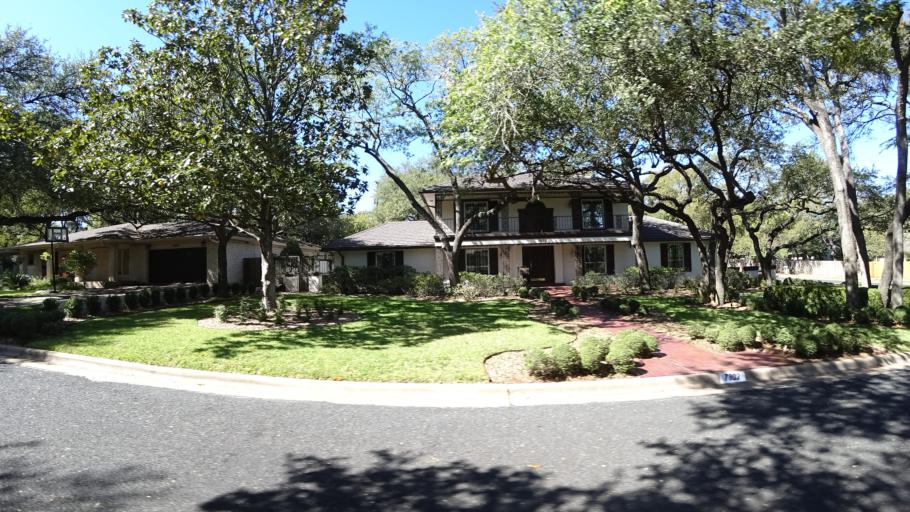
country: US
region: Texas
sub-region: Williamson County
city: Jollyville
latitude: 30.3673
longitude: -97.7587
